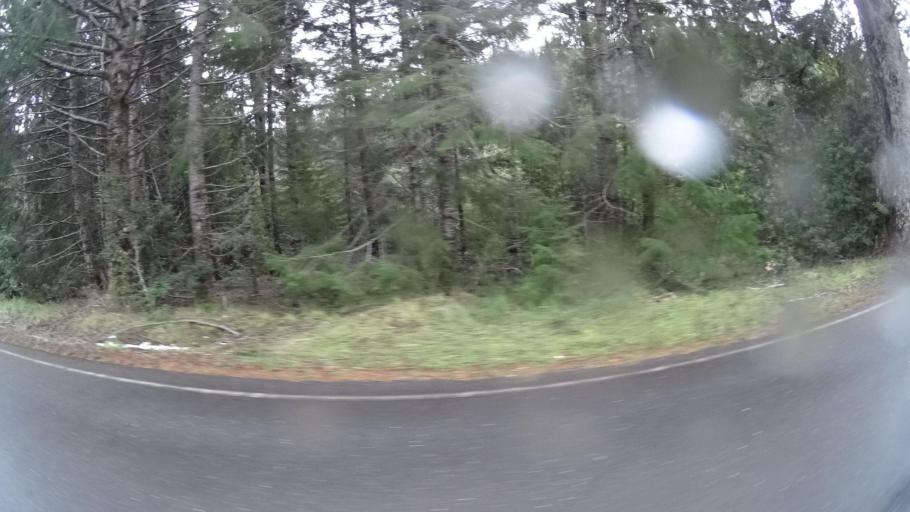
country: US
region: California
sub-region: Humboldt County
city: Willow Creek
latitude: 41.1665
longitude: -123.8161
